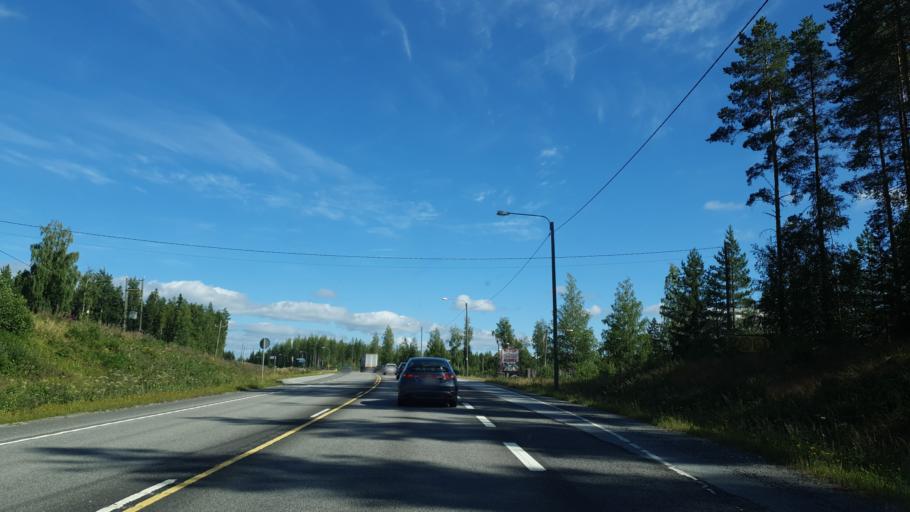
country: FI
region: Central Finland
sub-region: Jyvaeskylae
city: Toivakka
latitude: 62.2464
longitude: 26.0366
